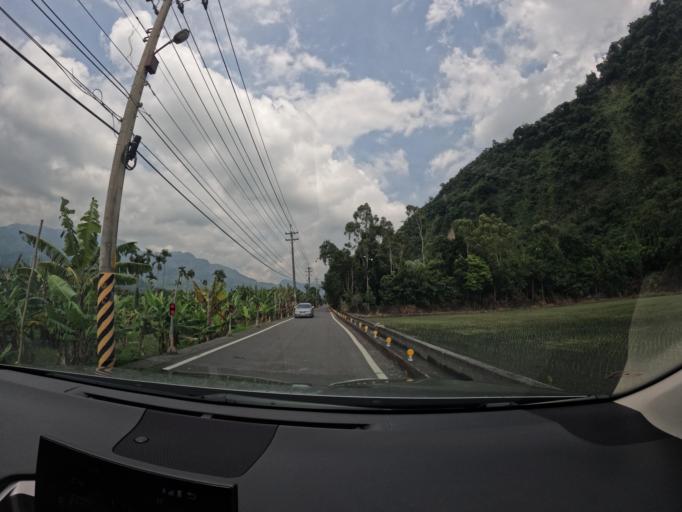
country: TW
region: Taiwan
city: Lugu
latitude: 23.8111
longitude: 120.8094
